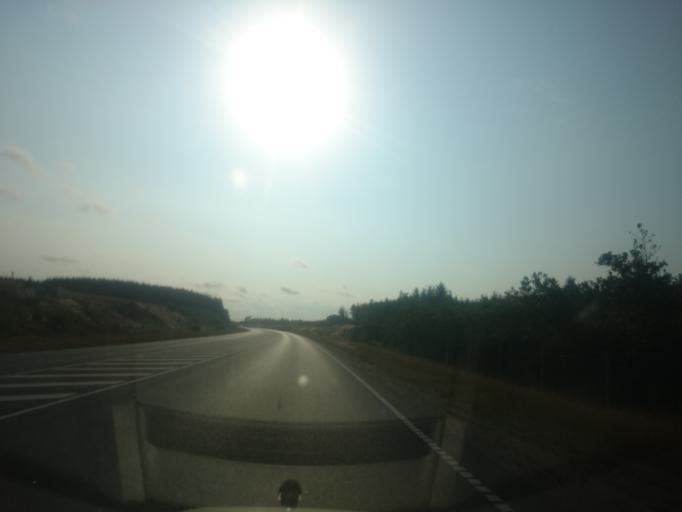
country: DK
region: South Denmark
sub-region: Vejle Kommune
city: Egtved
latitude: 55.7076
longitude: 9.2391
